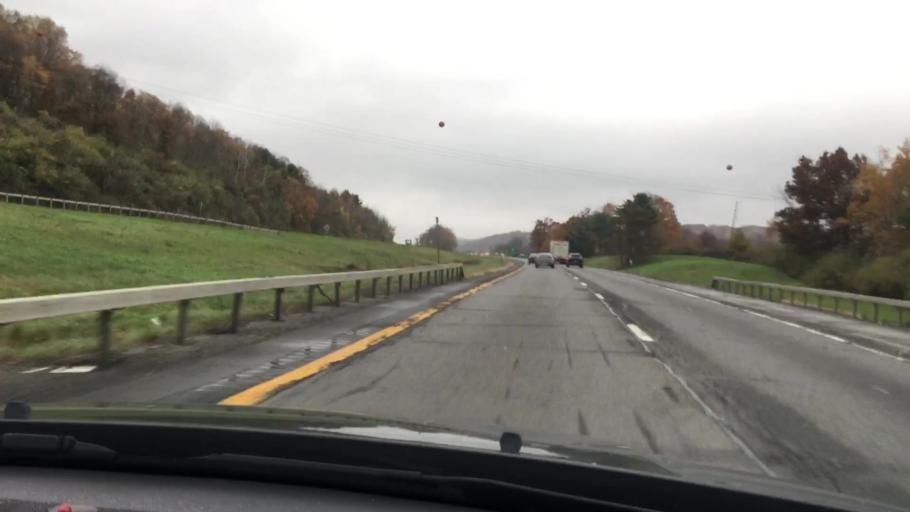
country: US
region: New York
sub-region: Putnam County
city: Lake Carmel
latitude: 41.4659
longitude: -73.6444
